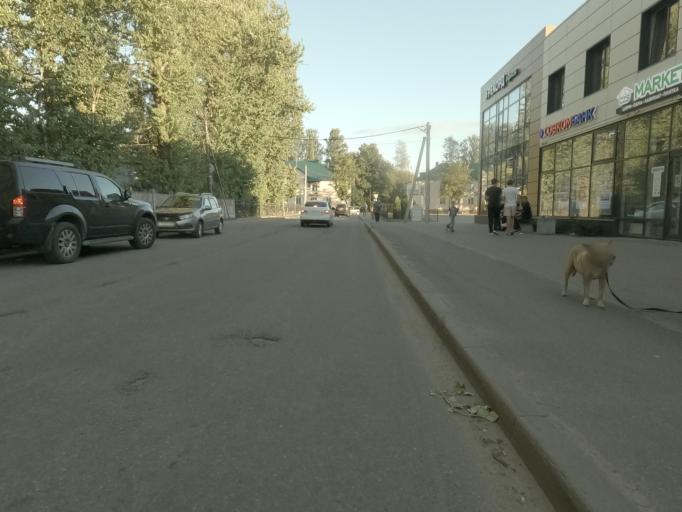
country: RU
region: Leningrad
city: Kirovsk
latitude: 59.8765
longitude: 30.9867
